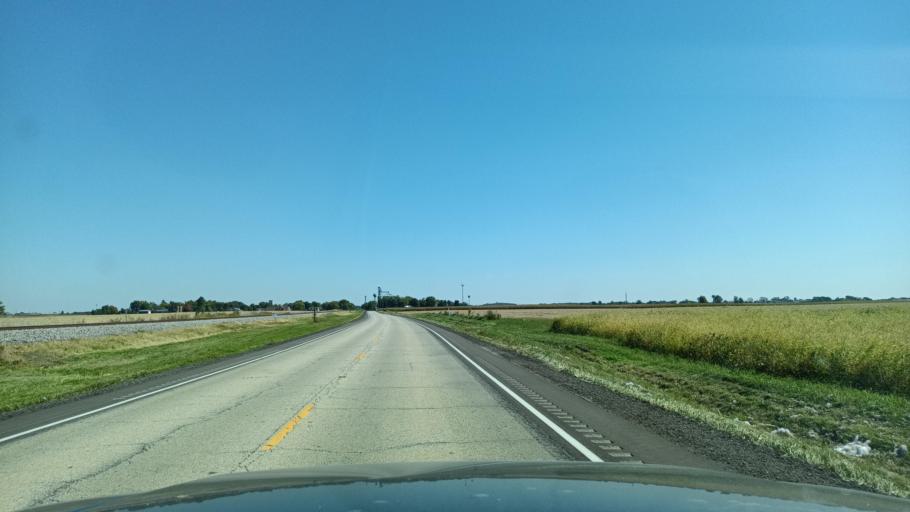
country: US
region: Illinois
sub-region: Woodford County
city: Eureka
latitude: 40.6270
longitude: -89.2952
